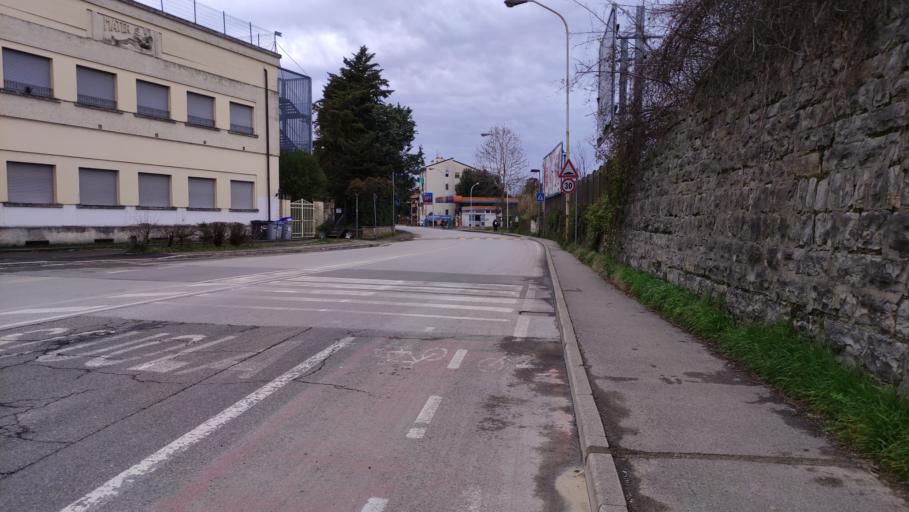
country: IT
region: Tuscany
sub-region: Province of Arezzo
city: Arezzo
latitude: 43.4641
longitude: 11.8694
